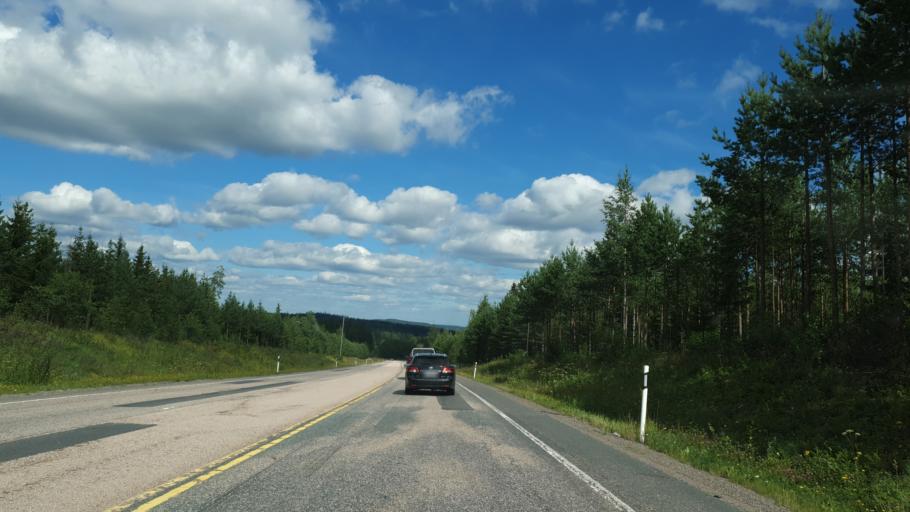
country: FI
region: Central Finland
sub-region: Jaemsae
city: Jaemsae
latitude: 61.8284
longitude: 25.0815
